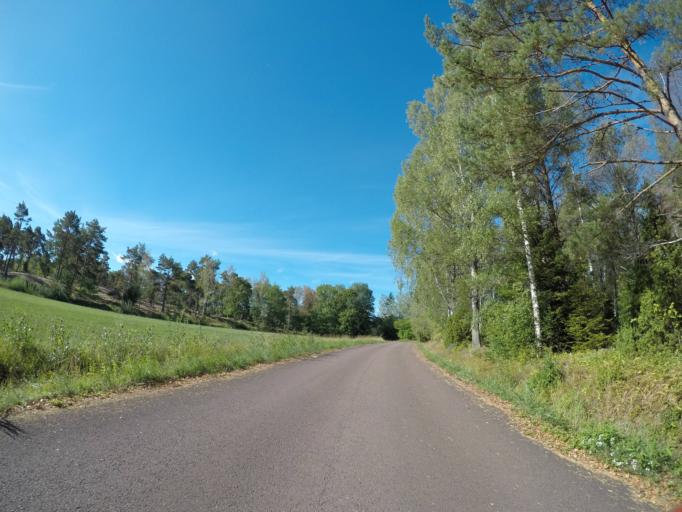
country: AX
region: Alands landsbygd
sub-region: Finstroem
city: Finstroem
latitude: 60.2994
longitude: 19.8823
